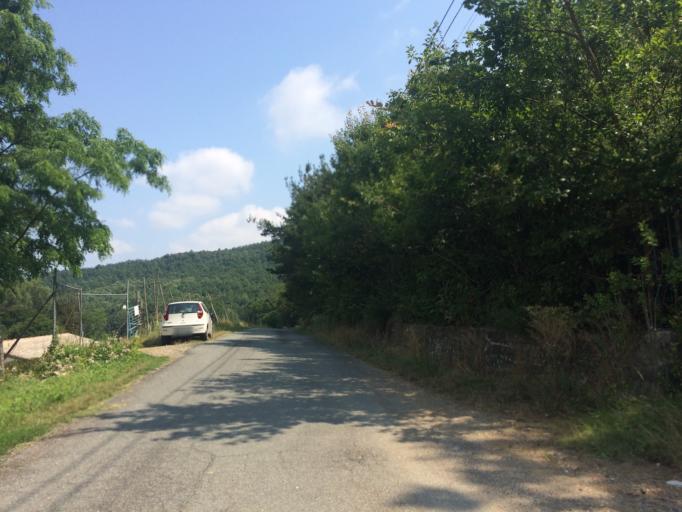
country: IT
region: Liguria
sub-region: Provincia di Savona
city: Molino-Pera
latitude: 44.4768
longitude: 8.3523
